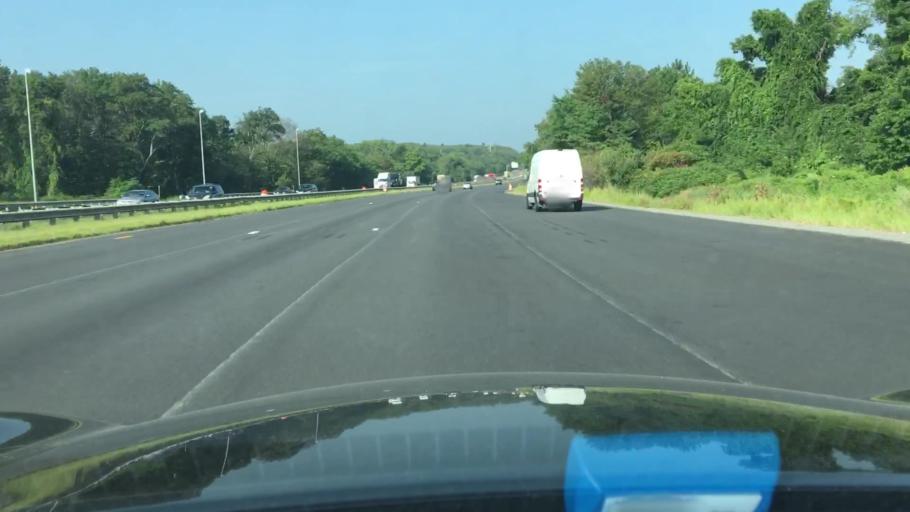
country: US
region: Massachusetts
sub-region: Worcester County
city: Millbury
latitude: 42.2062
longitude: -71.7898
